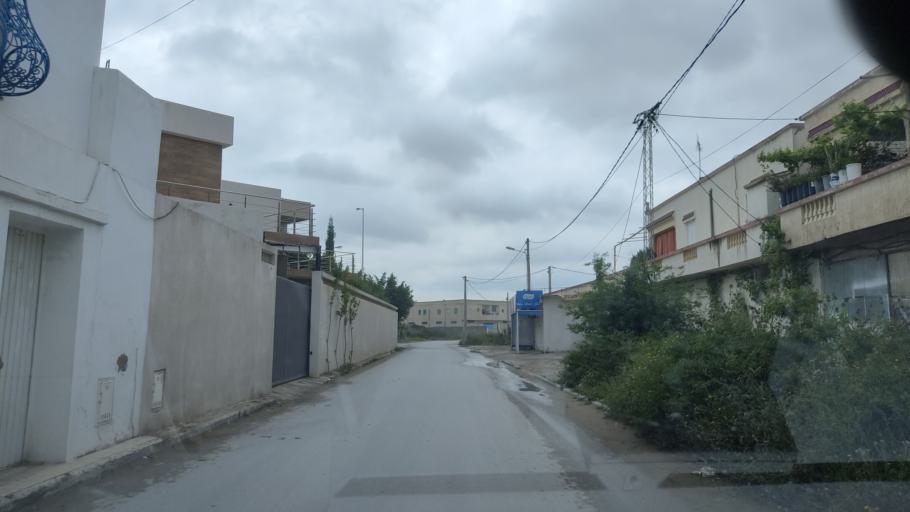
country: TN
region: Ariana
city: Ariana
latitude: 36.8822
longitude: 10.2190
